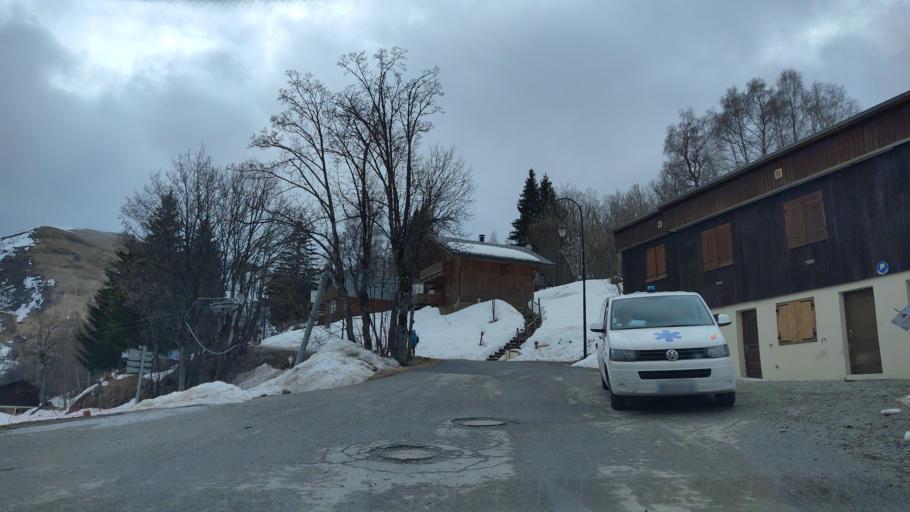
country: FR
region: Rhone-Alpes
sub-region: Departement de la Savoie
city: Saint-Jean-de-Maurienne
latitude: 45.2194
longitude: 6.2235
